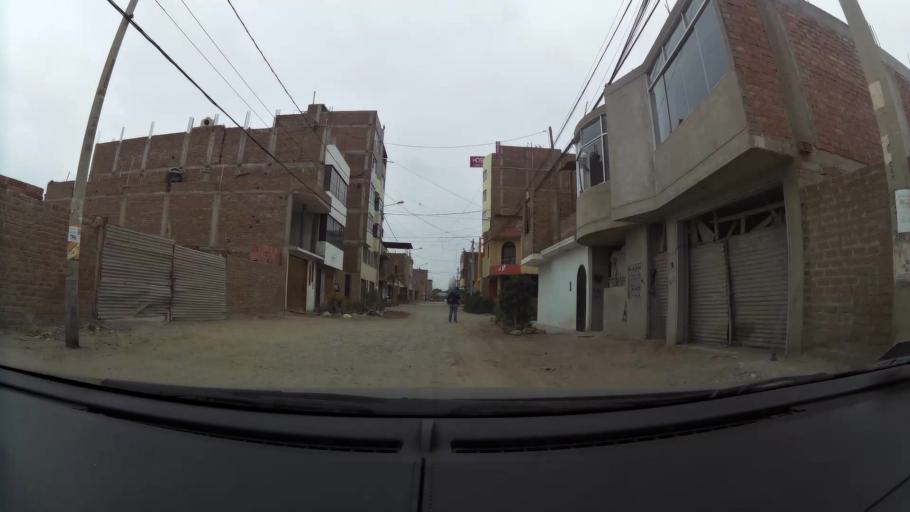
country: PE
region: La Libertad
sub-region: Provincia de Trujillo
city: Trujillo
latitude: -8.1159
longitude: -79.0468
